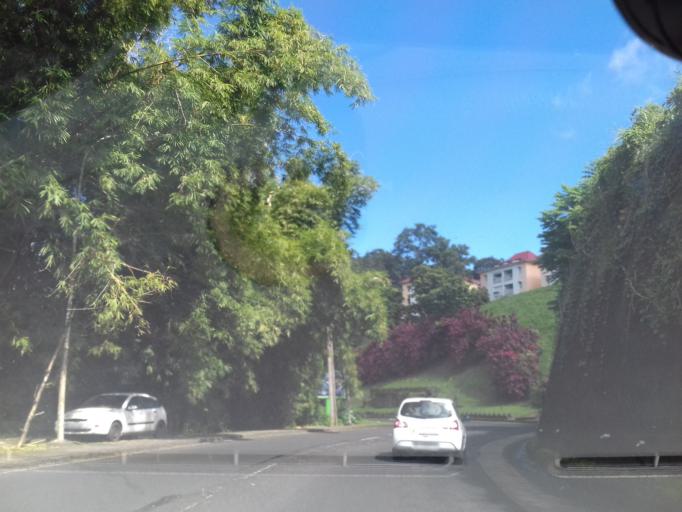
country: MQ
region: Martinique
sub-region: Martinique
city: Saint-Joseph
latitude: 14.6722
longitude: -61.0421
